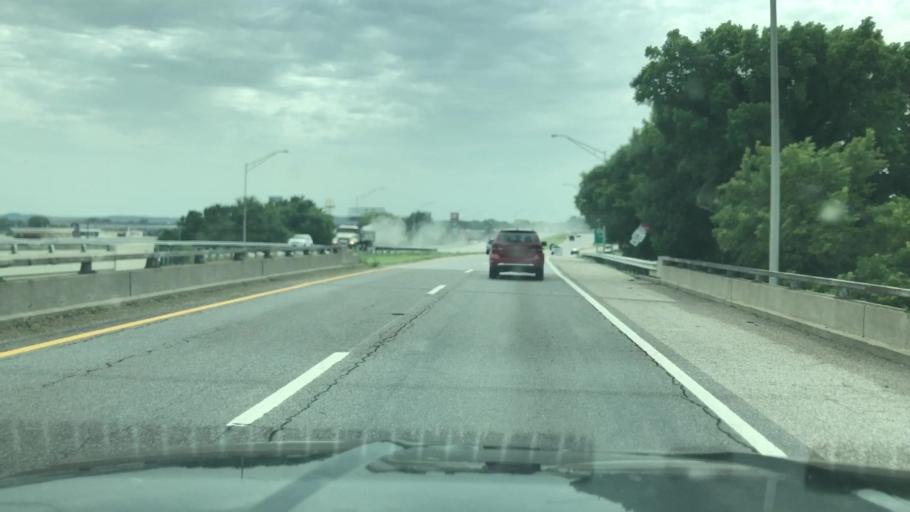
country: US
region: Oklahoma
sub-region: Tulsa County
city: Sand Springs
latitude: 36.1372
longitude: -96.1103
